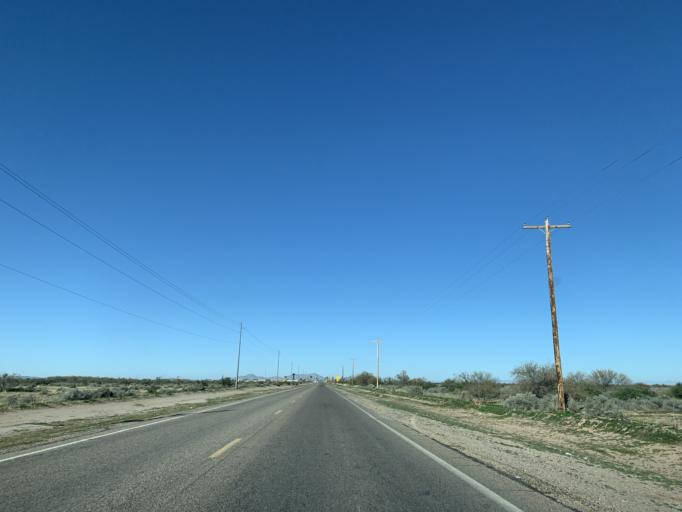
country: US
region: Arizona
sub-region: Pinal County
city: Arizona City
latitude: 32.7929
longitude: -111.6710
